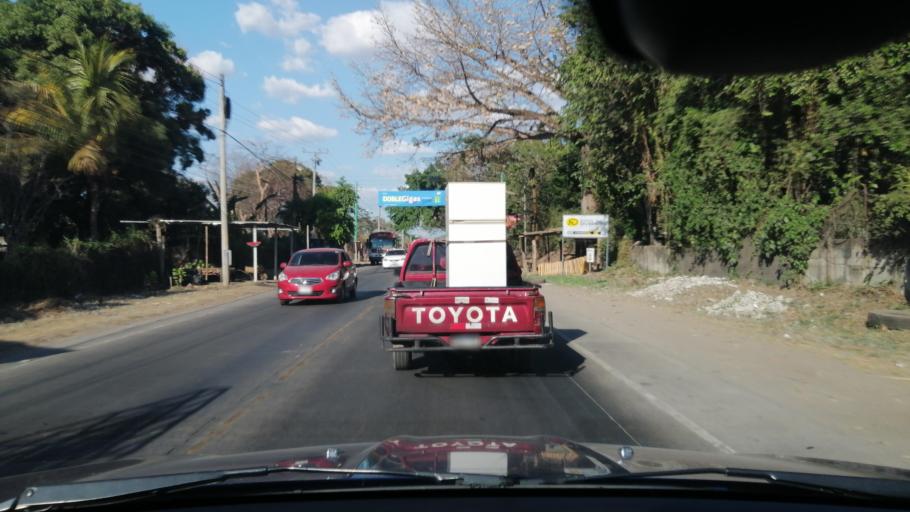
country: SV
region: Santa Ana
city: Santa Ana
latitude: 14.0130
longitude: -89.5418
